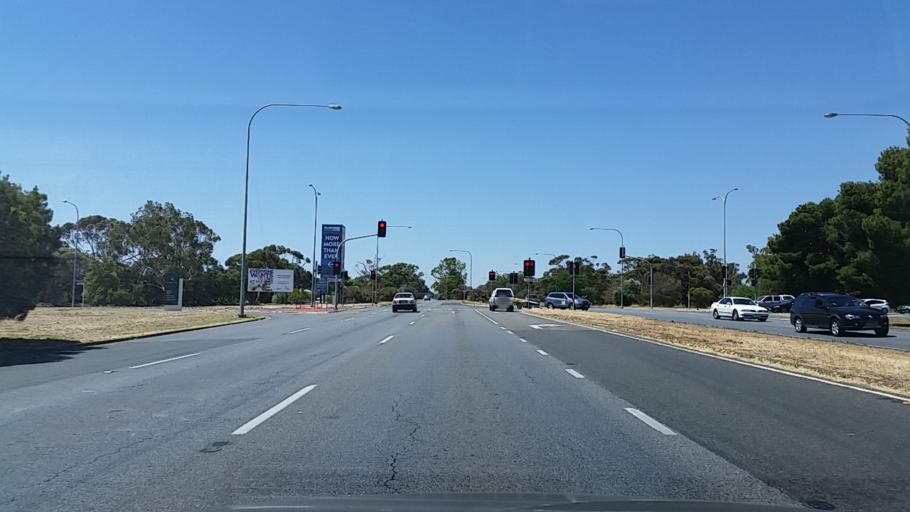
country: AU
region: South Australia
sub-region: Salisbury
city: Elizabeth
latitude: -34.7079
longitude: 138.6781
